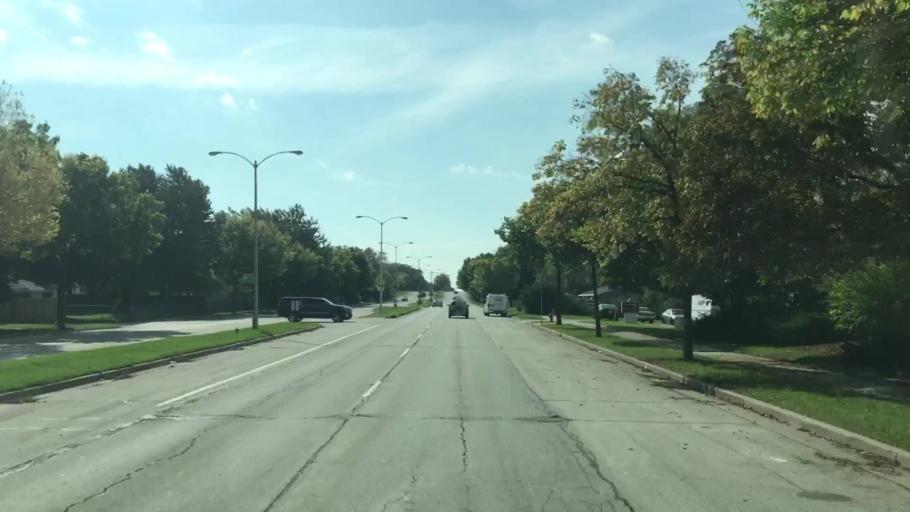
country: US
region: Wisconsin
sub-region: Waukesha County
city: Butler
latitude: 43.1691
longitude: -88.0445
